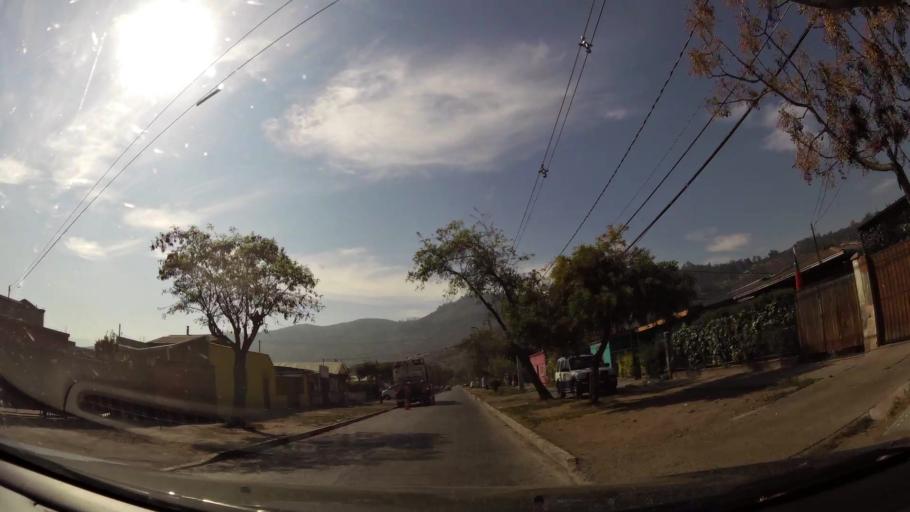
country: CL
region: Santiago Metropolitan
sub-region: Provincia de Santiago
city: Santiago
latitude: -33.4064
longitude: -70.6295
